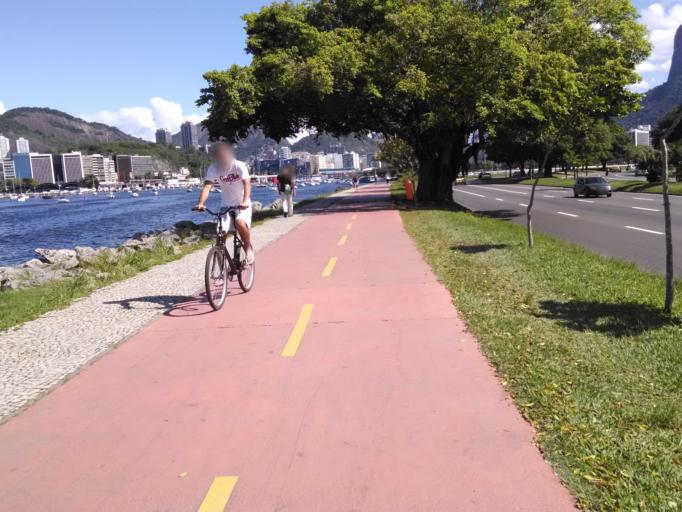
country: BR
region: Rio de Janeiro
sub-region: Rio De Janeiro
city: Rio de Janeiro
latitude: -22.9432
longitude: -43.1730
